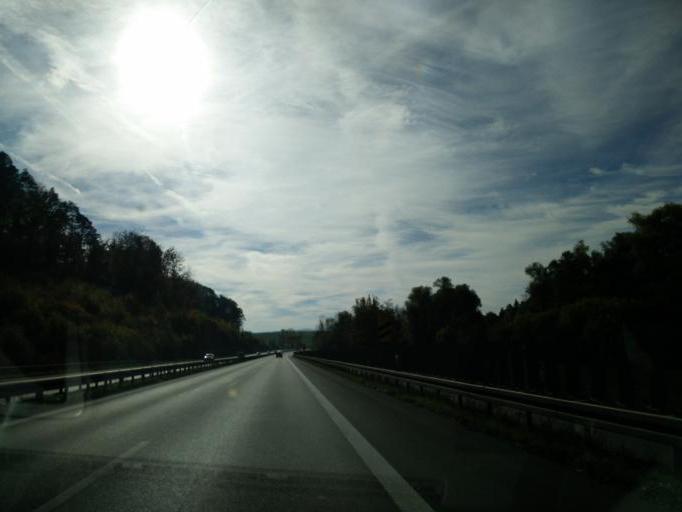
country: DE
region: Baden-Wuerttemberg
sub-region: Tuebingen Region
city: Dusslingen
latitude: 48.4764
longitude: 9.0648
